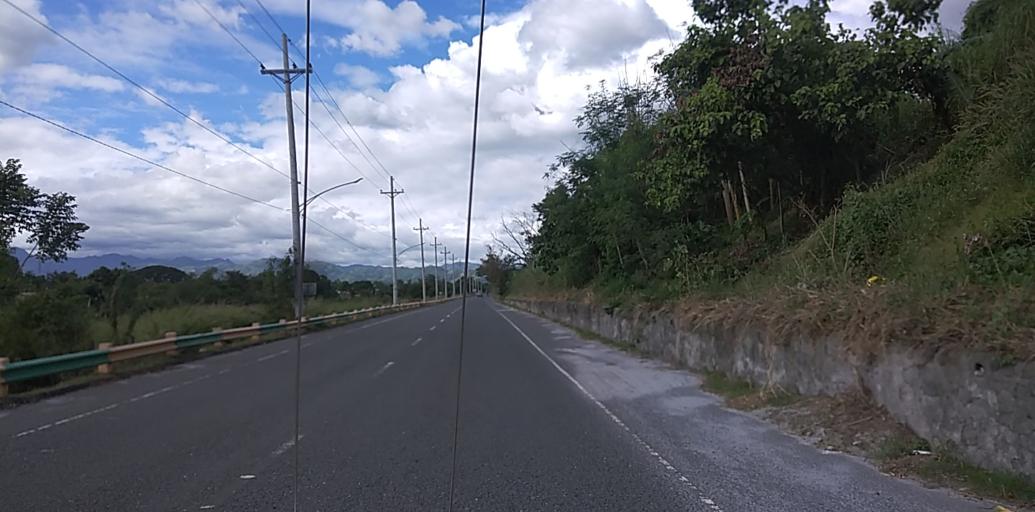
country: PH
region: Central Luzon
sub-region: Province of Pampanga
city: Dolores
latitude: 15.0953
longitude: 120.5300
